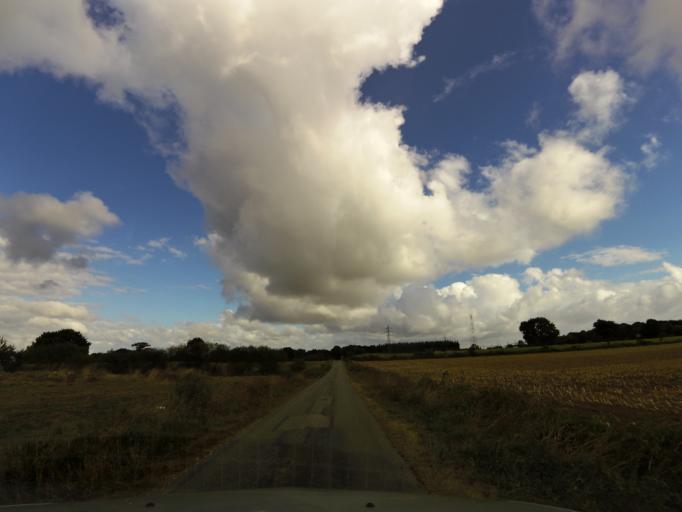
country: FR
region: Brittany
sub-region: Departement d'Ille-et-Vilaine
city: Crevin
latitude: 47.9353
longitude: -1.6425
